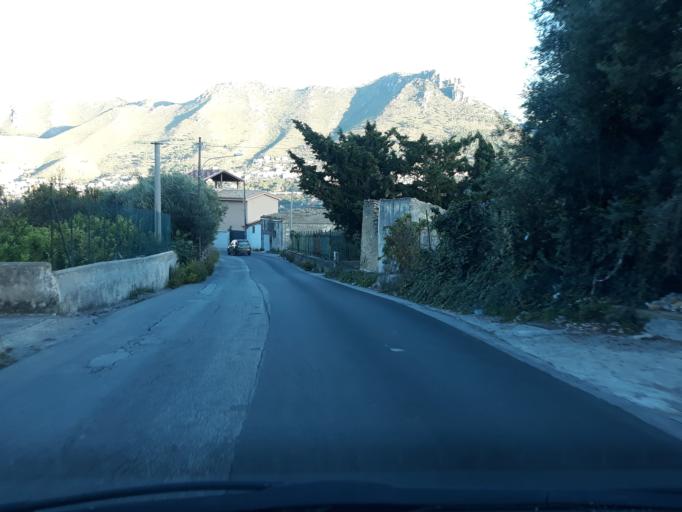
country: IT
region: Sicily
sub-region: Palermo
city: Monreale
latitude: 38.0729
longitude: 13.2927
